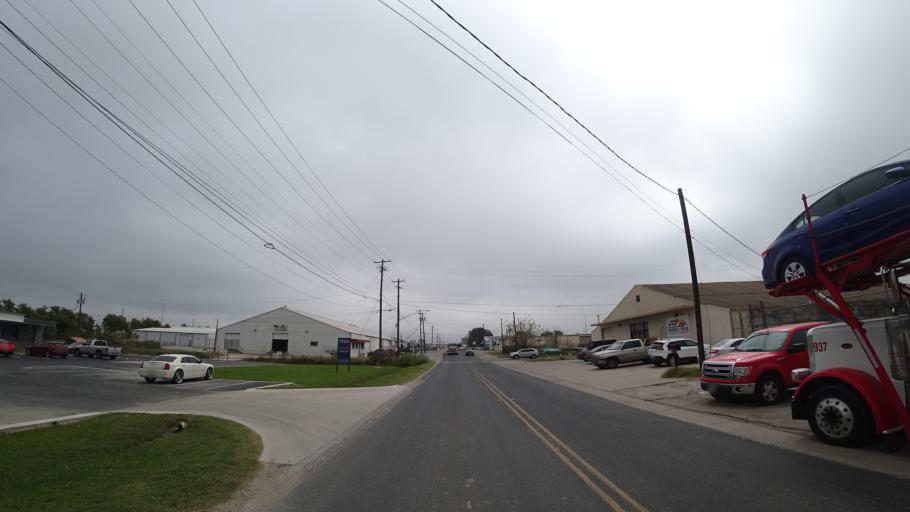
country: US
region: Texas
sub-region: Travis County
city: Austin
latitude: 30.2189
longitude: -97.7626
